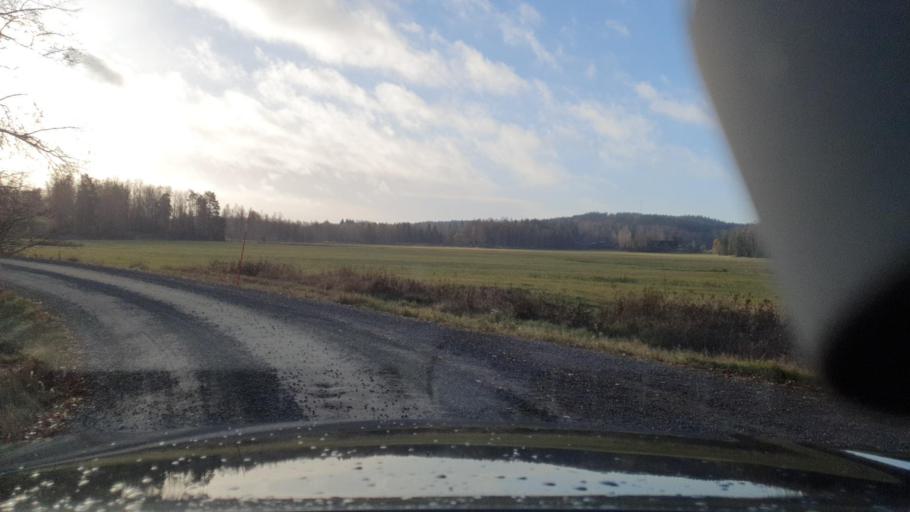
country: SE
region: Vaermland
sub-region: Grums Kommun
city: Grums
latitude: 59.4883
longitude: 12.9293
